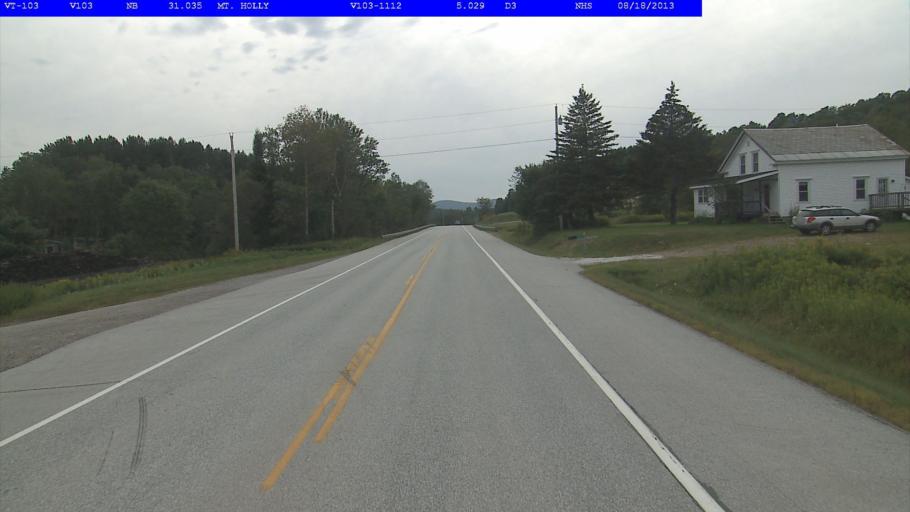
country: US
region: Vermont
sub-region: Rutland County
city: Rutland
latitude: 43.4481
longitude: -72.8212
